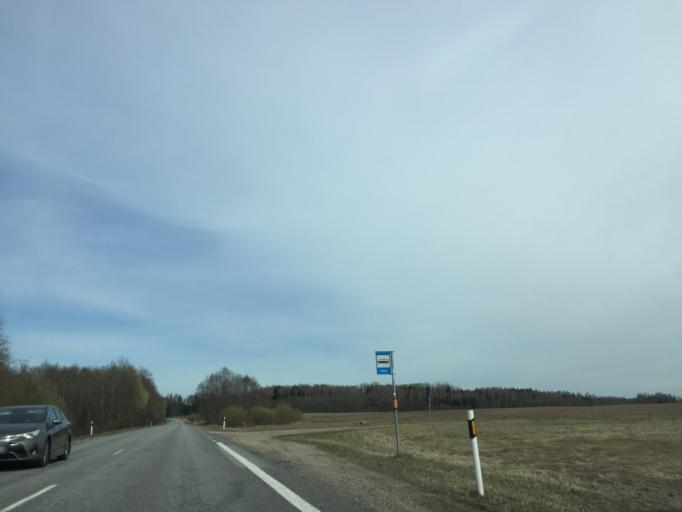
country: EE
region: Vorumaa
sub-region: Antsla vald
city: Vana-Antsla
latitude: 57.9331
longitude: 26.3518
